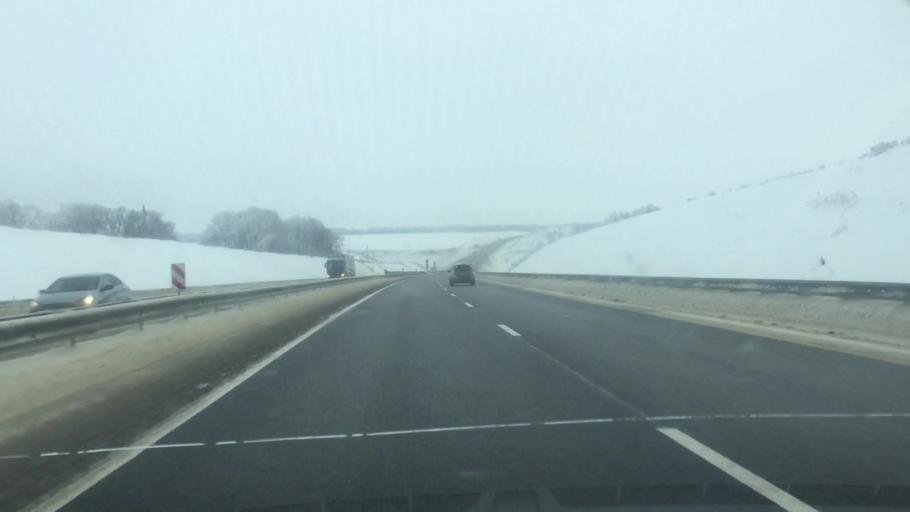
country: RU
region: Lipetsk
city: Stanovoye
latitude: 52.8722
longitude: 38.2791
